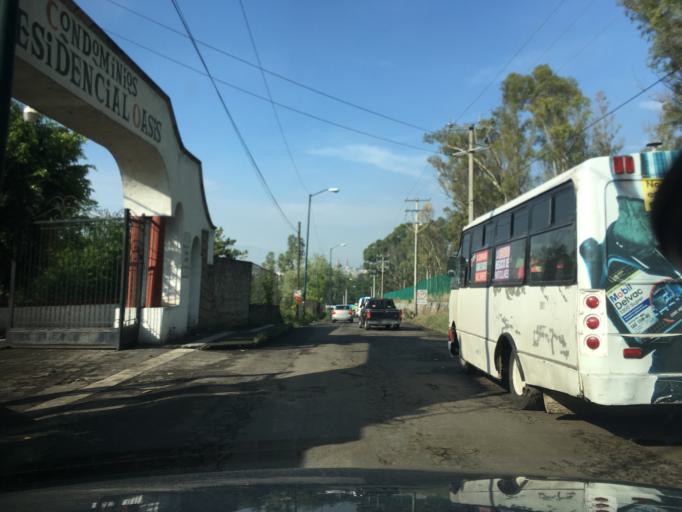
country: MX
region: Michoacan
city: Morelia
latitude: 19.7216
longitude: -101.1831
